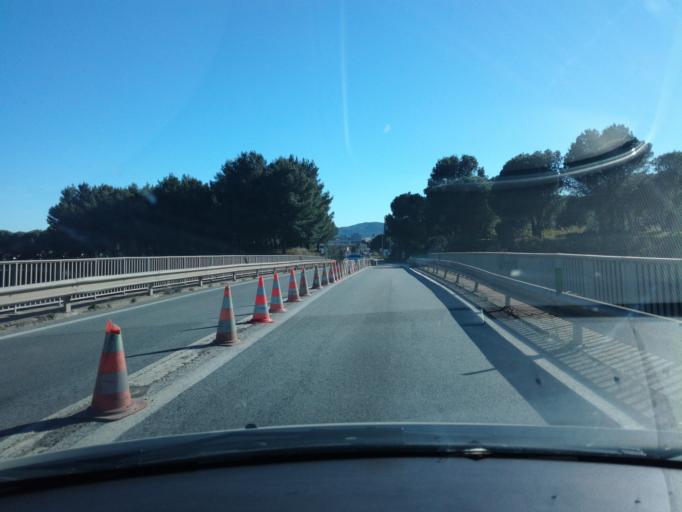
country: FR
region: Provence-Alpes-Cote d'Azur
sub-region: Departement du Var
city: Puget-sur-Argens
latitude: 43.4593
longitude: 6.6893
